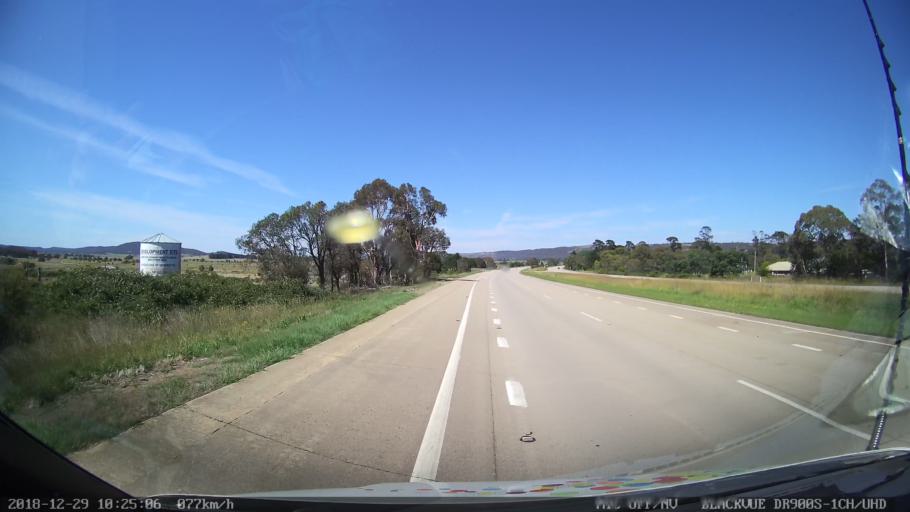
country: AU
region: New South Wales
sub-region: Yass Valley
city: Gundaroo
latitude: -34.9165
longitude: 149.4385
